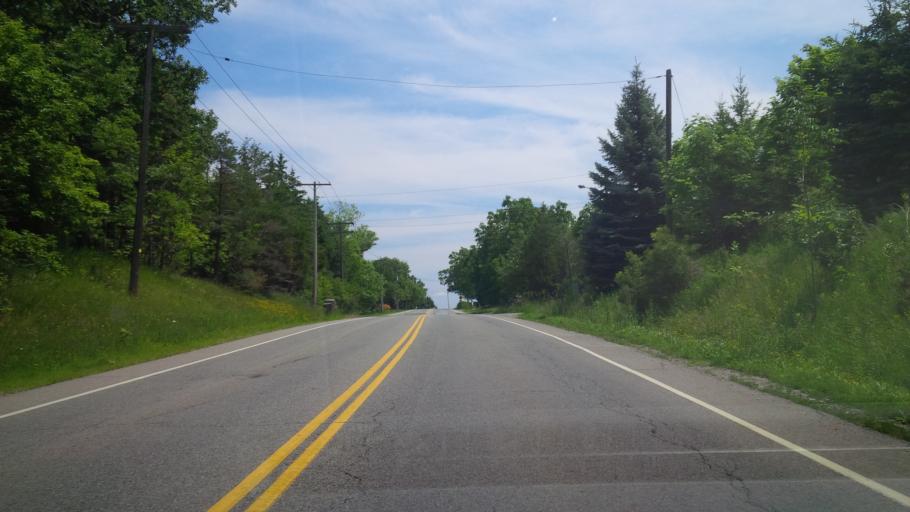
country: CA
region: Ontario
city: Burlington
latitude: 43.4222
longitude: -79.8292
